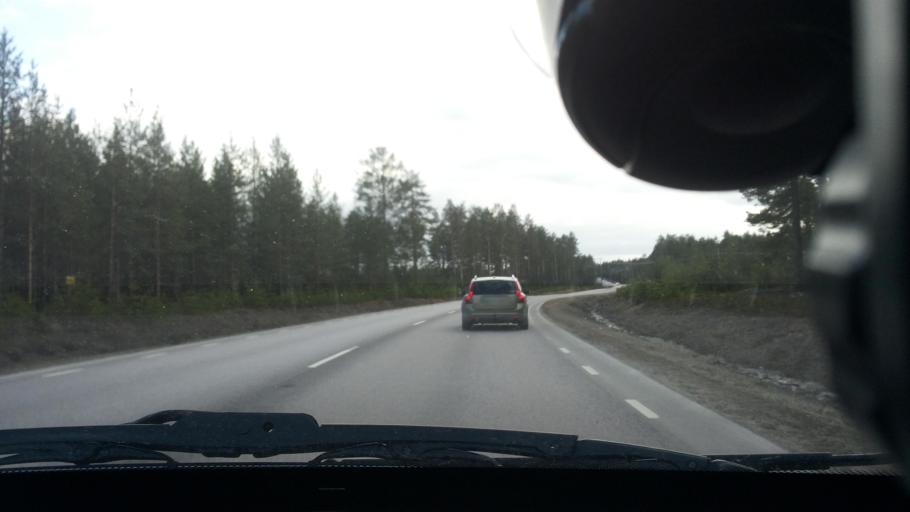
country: SE
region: Norrbotten
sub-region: Lulea Kommun
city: Gammelstad
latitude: 65.6131
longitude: 22.0436
